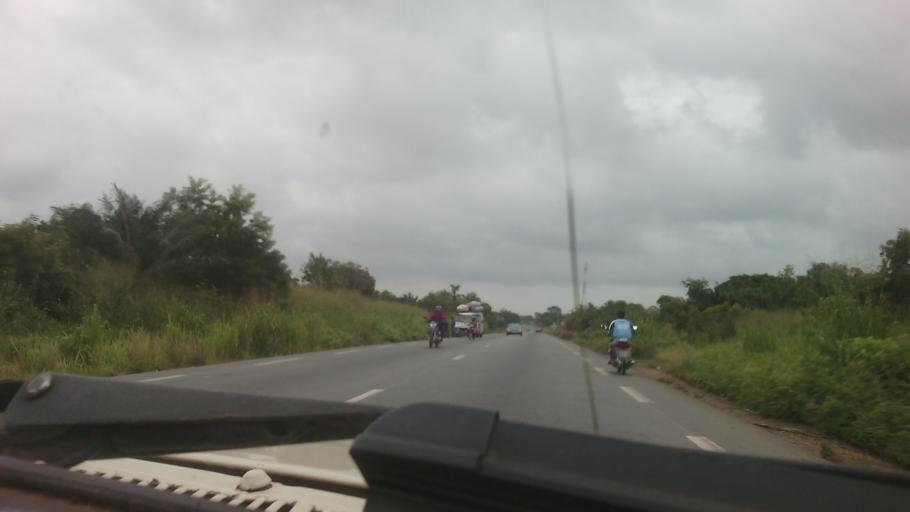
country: BJ
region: Atlantique
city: Ouidah
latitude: 6.3922
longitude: 1.9909
